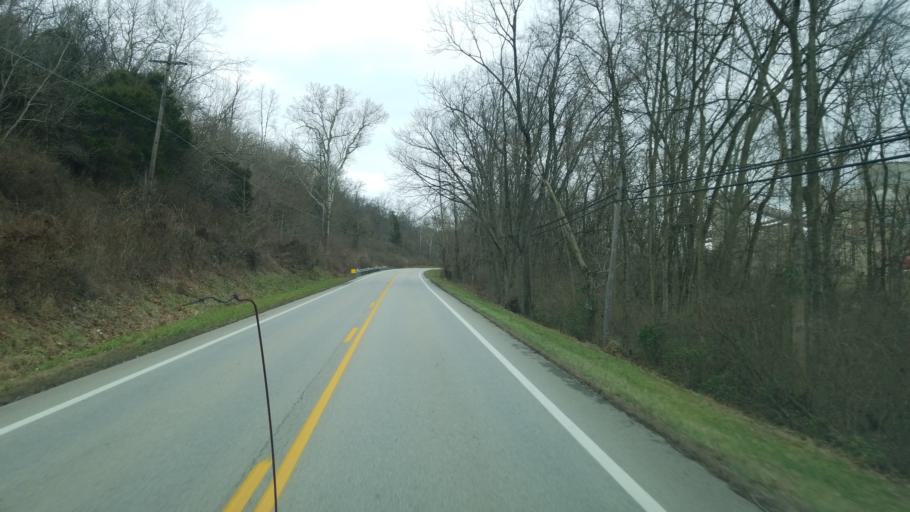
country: US
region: Ohio
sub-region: Clermont County
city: New Richmond
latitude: 38.8746
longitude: -84.2254
